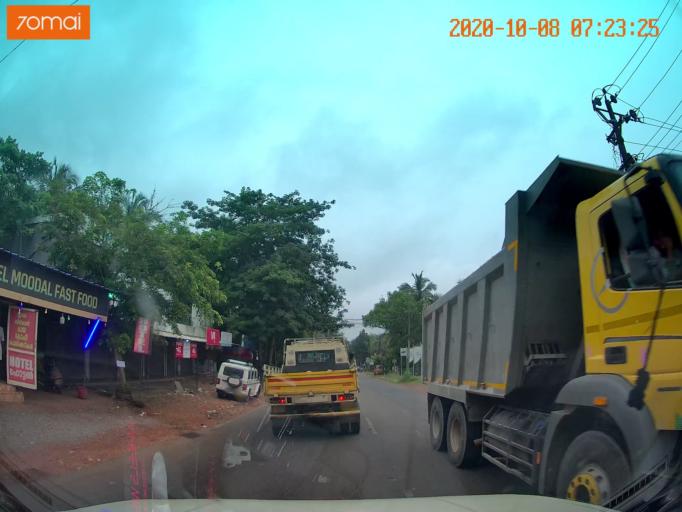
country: IN
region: Kerala
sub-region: Malappuram
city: Tirur
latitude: 10.8680
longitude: 76.0455
